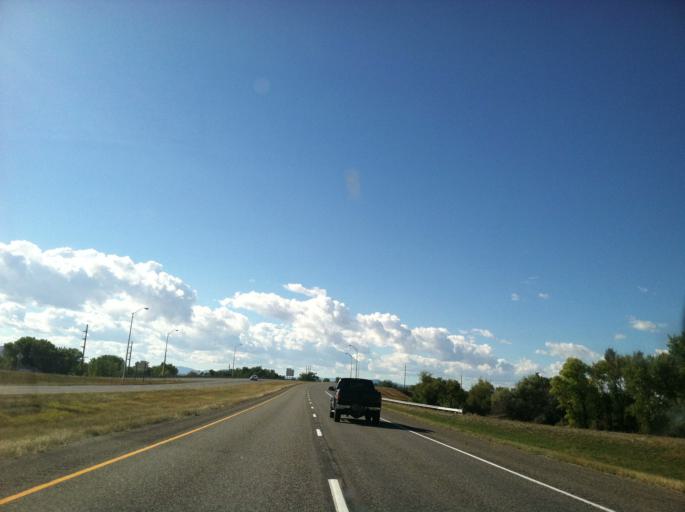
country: US
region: Montana
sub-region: Gallatin County
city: Three Forks
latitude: 45.9022
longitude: -111.5359
